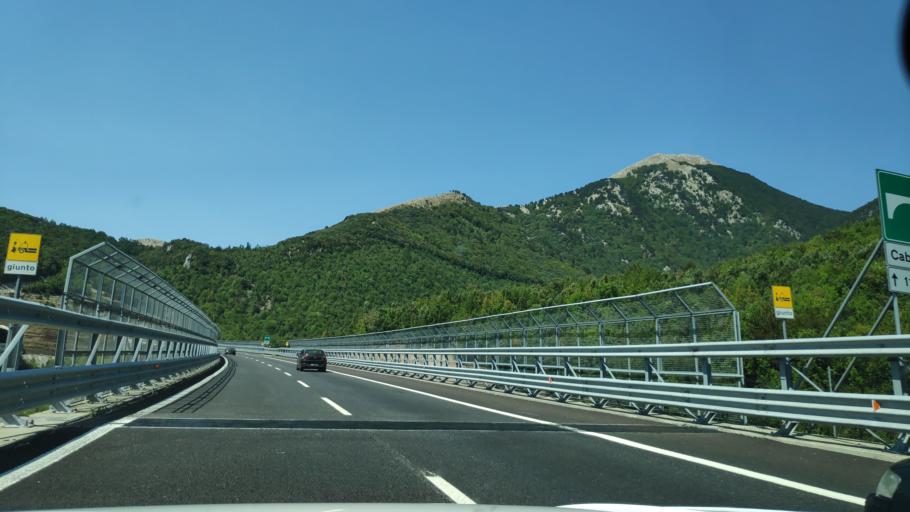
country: IT
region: Calabria
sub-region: Provincia di Cosenza
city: Morano Calabro
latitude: 39.8898
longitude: 16.1443
